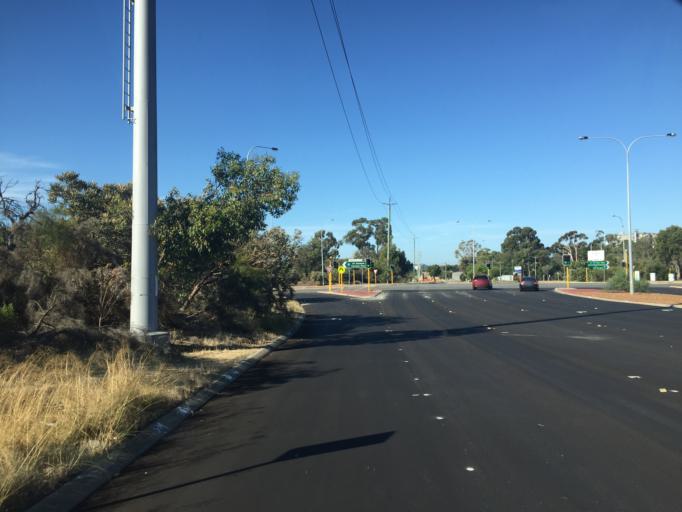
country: AU
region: Western Australia
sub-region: Canning
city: East Cannington
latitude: -31.9987
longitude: 115.9628
